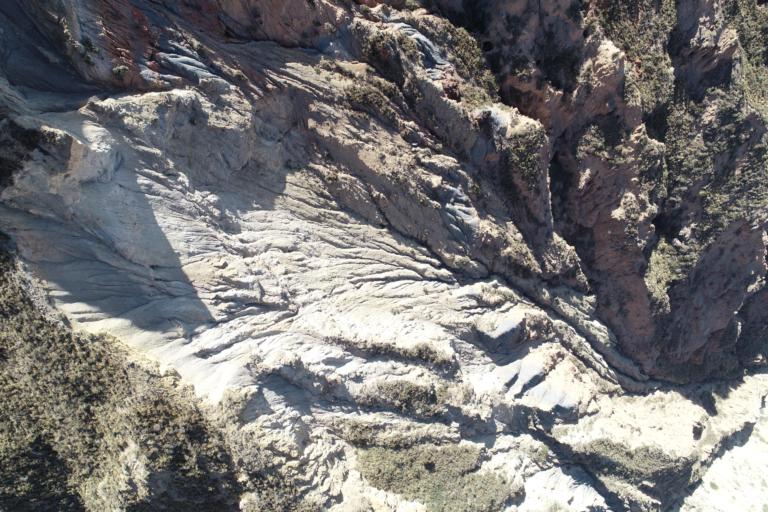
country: BO
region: La Paz
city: La Paz
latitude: -16.5532
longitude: -68.1040
